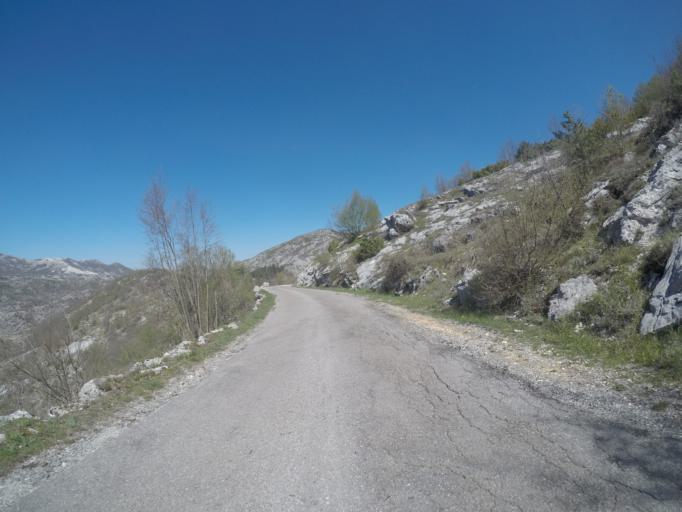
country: ME
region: Cetinje
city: Cetinje
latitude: 42.4523
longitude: 18.8735
